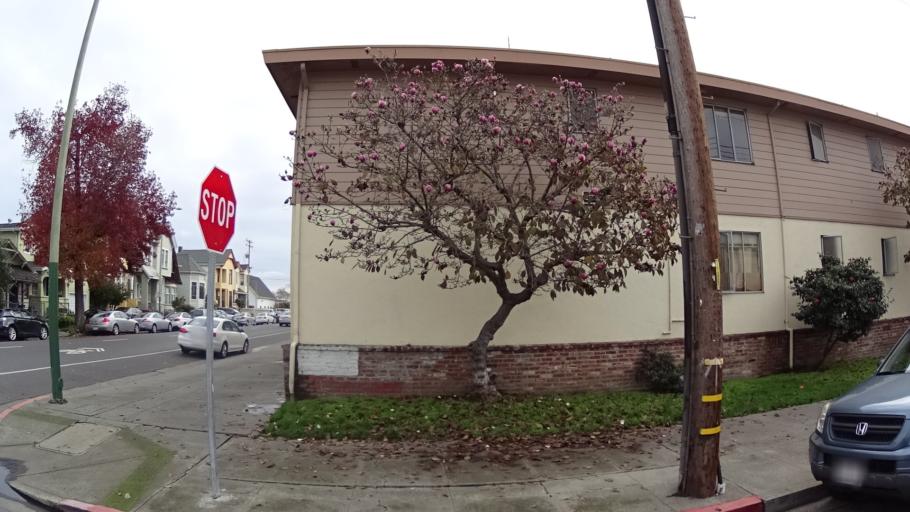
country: US
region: California
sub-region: Alameda County
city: Oakland
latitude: 37.7948
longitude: -122.2515
